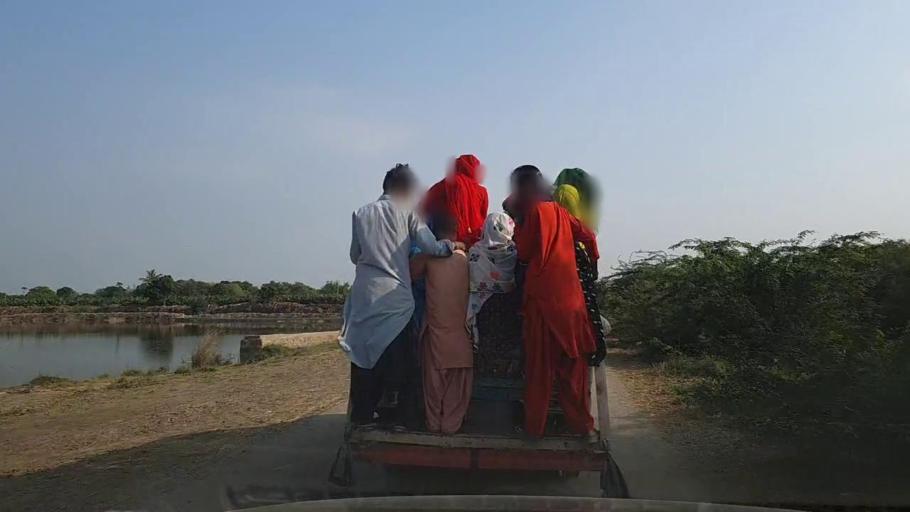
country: PK
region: Sindh
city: Thatta
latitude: 24.6457
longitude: 67.9312
